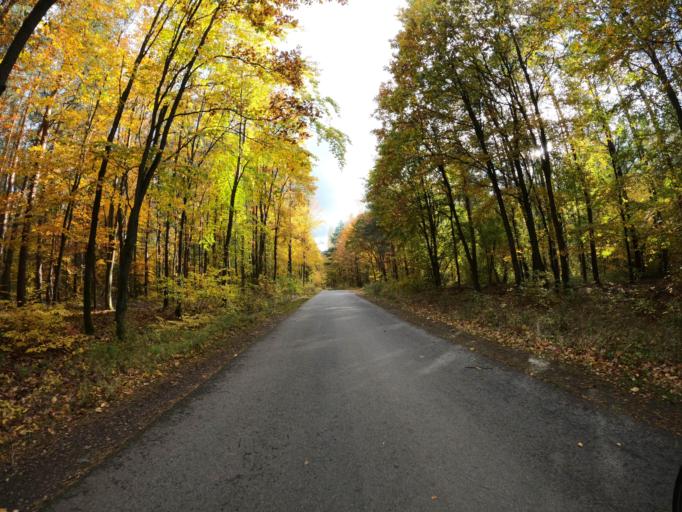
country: PL
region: West Pomeranian Voivodeship
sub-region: Powiat mysliborski
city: Barlinek
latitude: 52.9360
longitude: 15.2849
